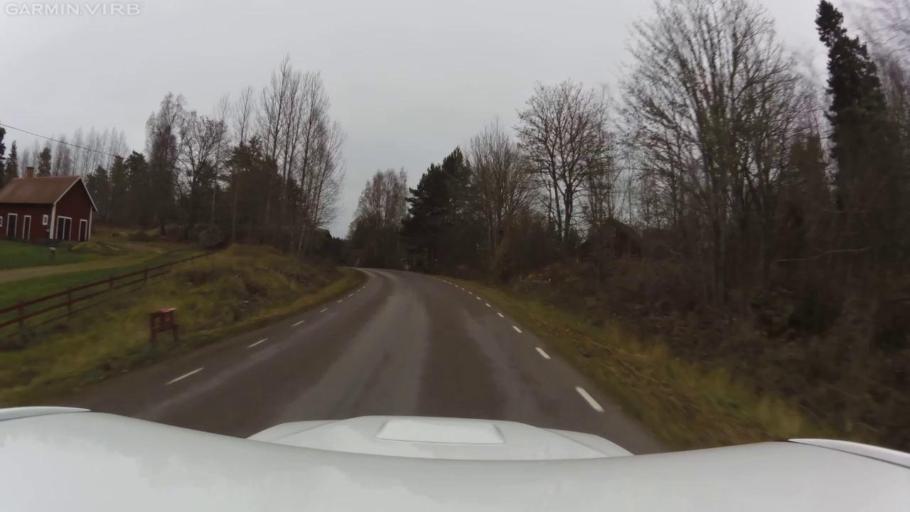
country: SE
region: OEstergoetland
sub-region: Linkopings Kommun
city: Vikingstad
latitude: 58.2525
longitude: 15.3842
